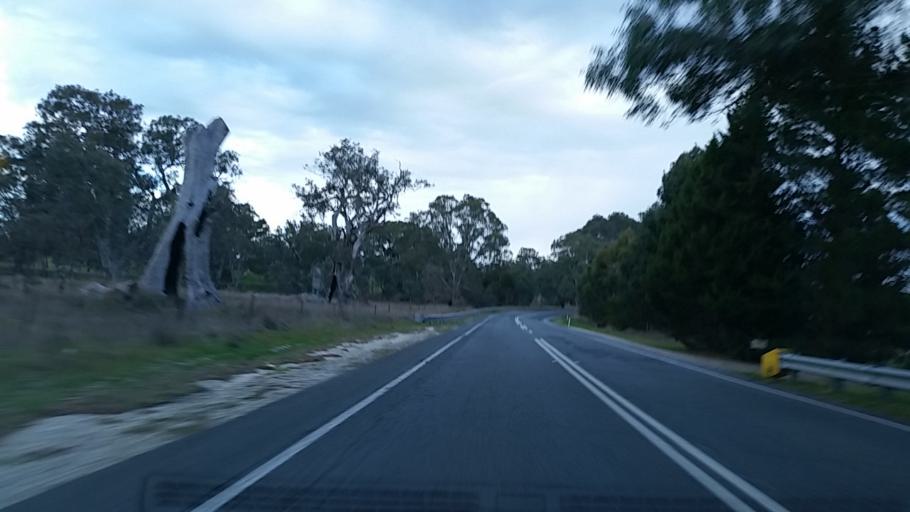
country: AU
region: South Australia
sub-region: Adelaide Hills
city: Birdwood
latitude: -34.8029
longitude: 138.9927
